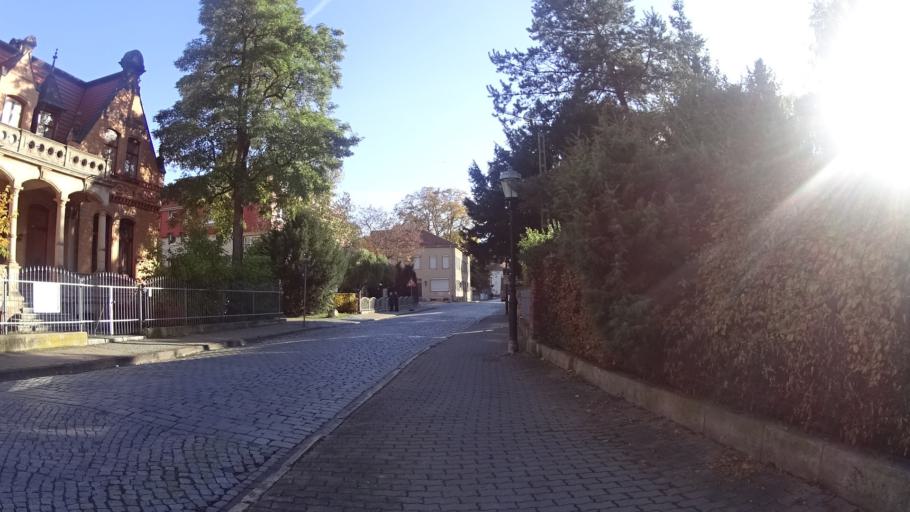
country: DE
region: Thuringia
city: Arnstadt
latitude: 50.8309
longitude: 10.9480
